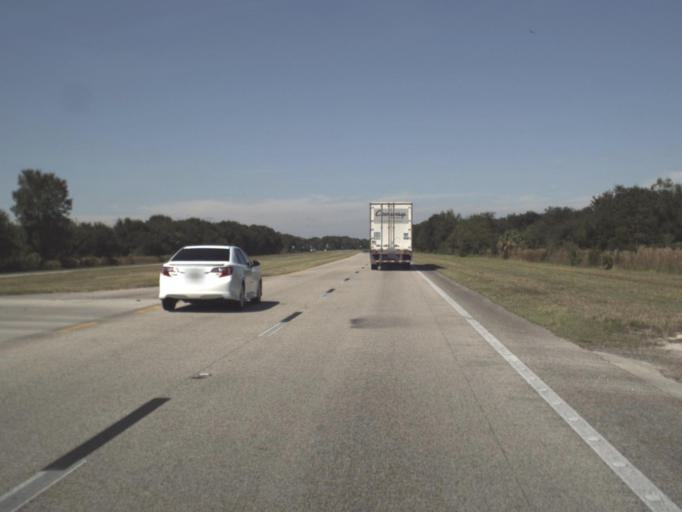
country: US
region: Florida
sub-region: Highlands County
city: Placid Lakes
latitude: 27.0222
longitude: -81.3389
